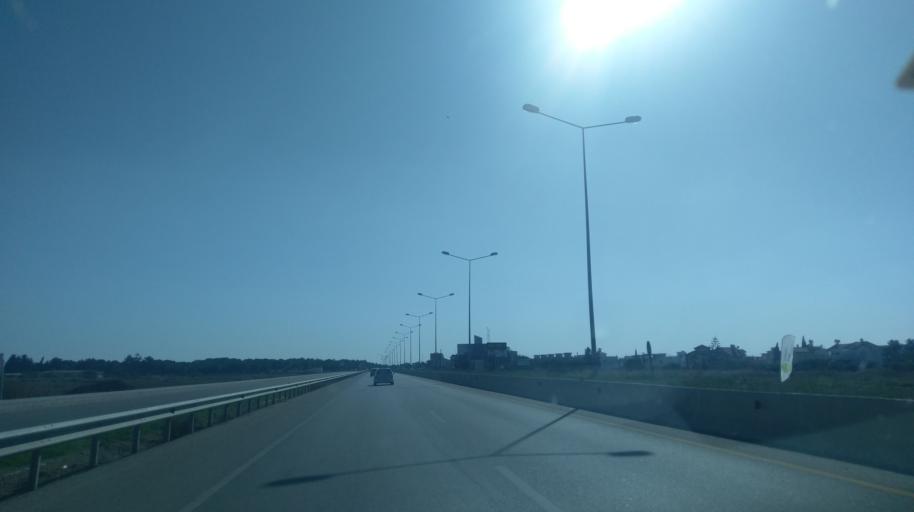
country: CY
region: Ammochostos
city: Trikomo
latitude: 35.2096
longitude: 33.8939
